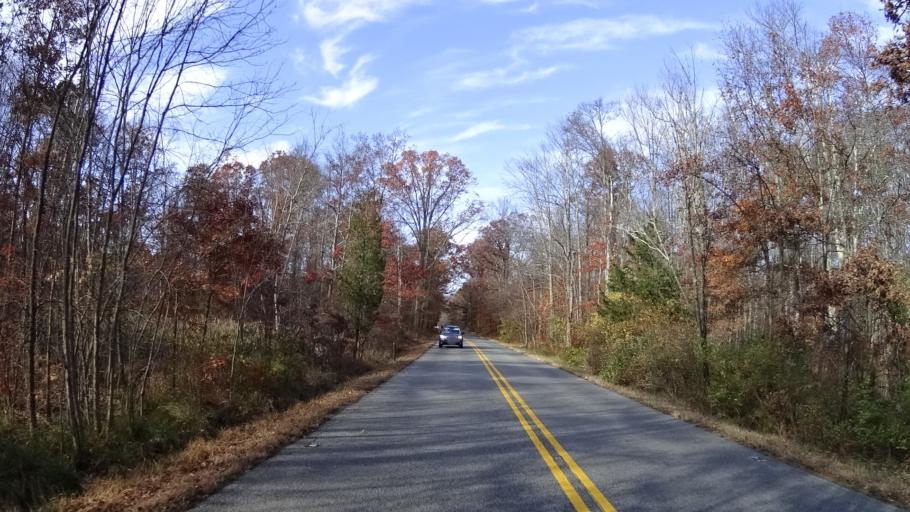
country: US
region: New Jersey
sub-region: Union County
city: Berkeley Heights
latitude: 40.7247
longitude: -74.4938
